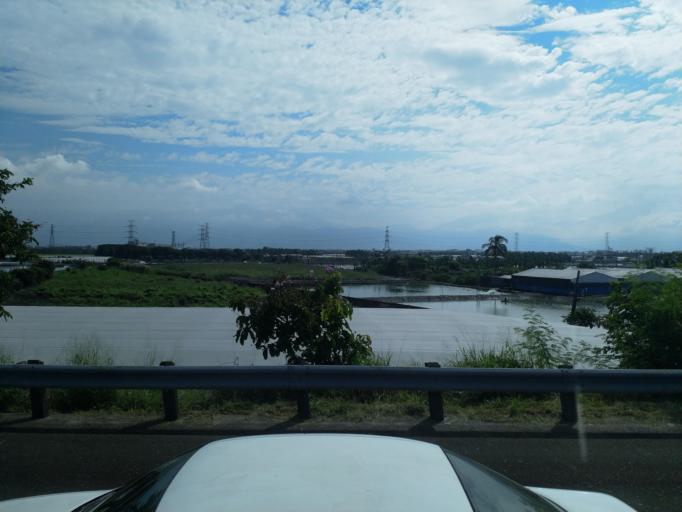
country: TW
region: Taiwan
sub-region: Pingtung
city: Pingtung
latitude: 22.8175
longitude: 120.4868
